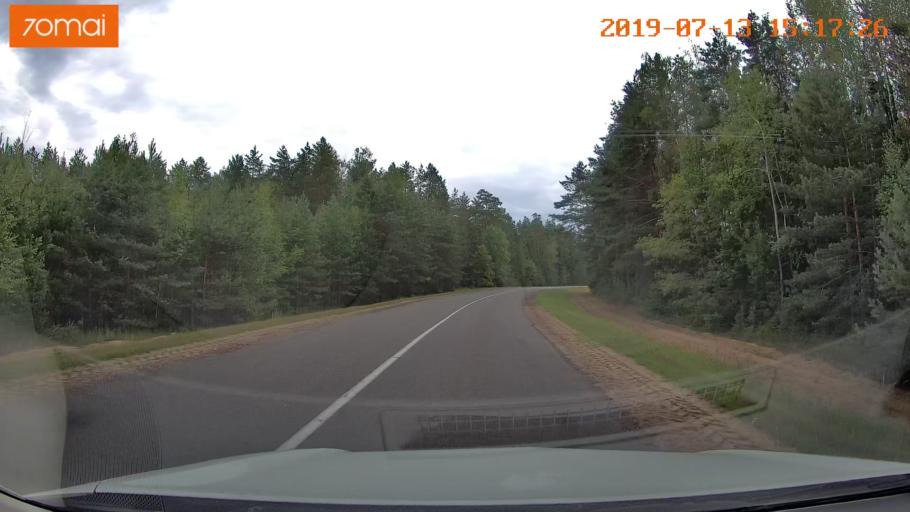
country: BY
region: Mogilev
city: Hlusha
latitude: 53.0960
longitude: 28.8445
